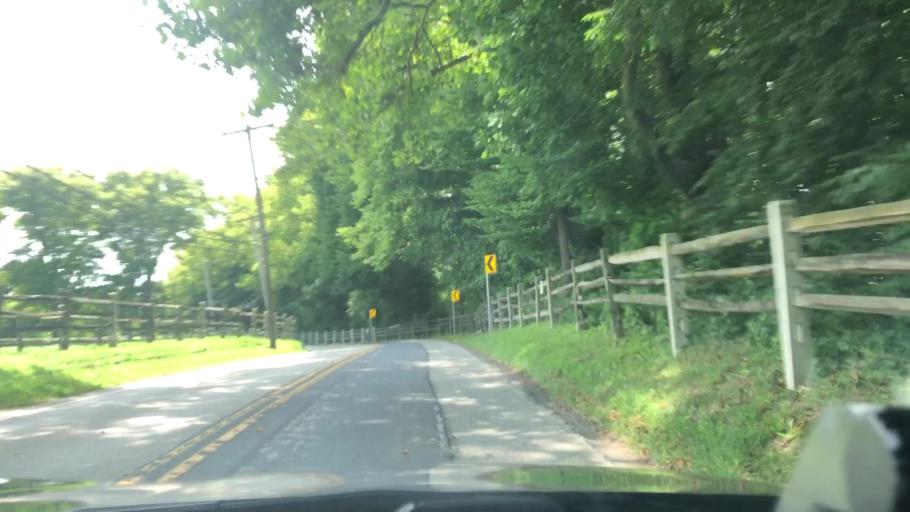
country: US
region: Pennsylvania
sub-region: Montgomery County
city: Flourtown
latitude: 40.1010
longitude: -75.2297
